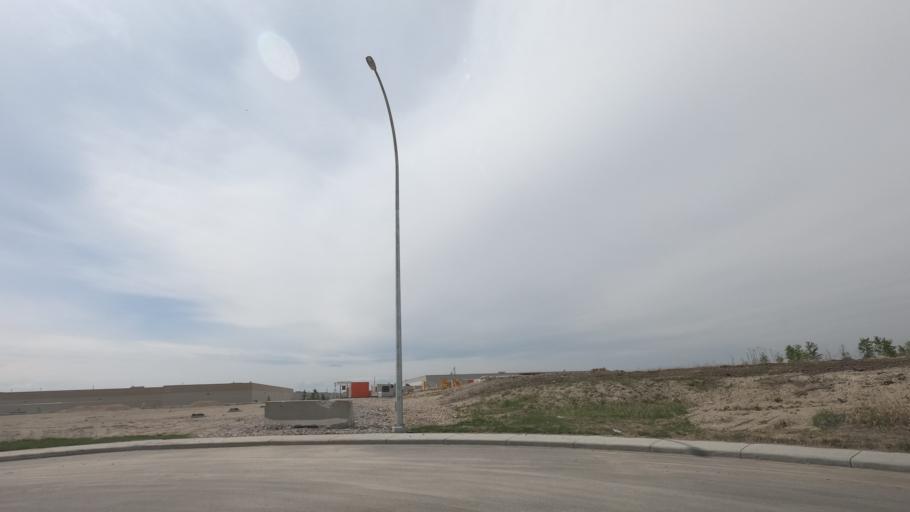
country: CA
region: Alberta
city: Airdrie
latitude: 51.3059
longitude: -113.9847
